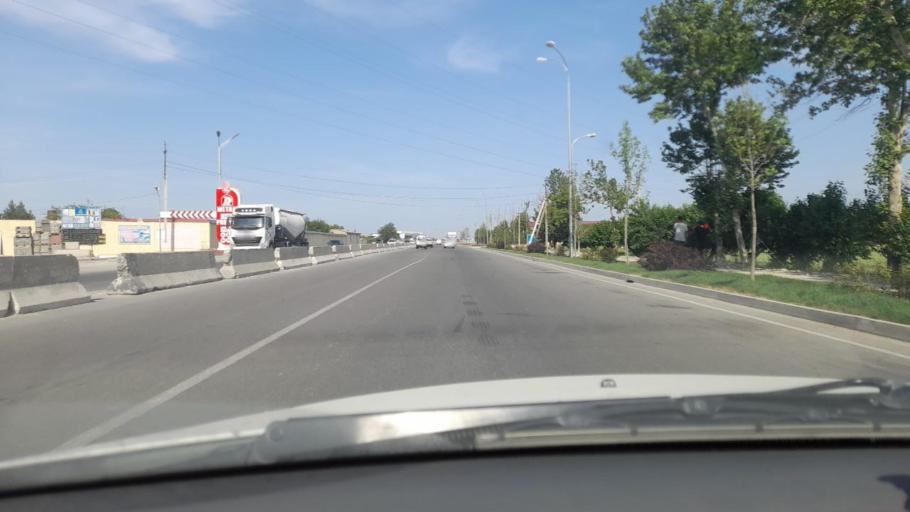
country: UZ
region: Samarqand
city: Samarqand
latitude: 39.7106
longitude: 66.9685
